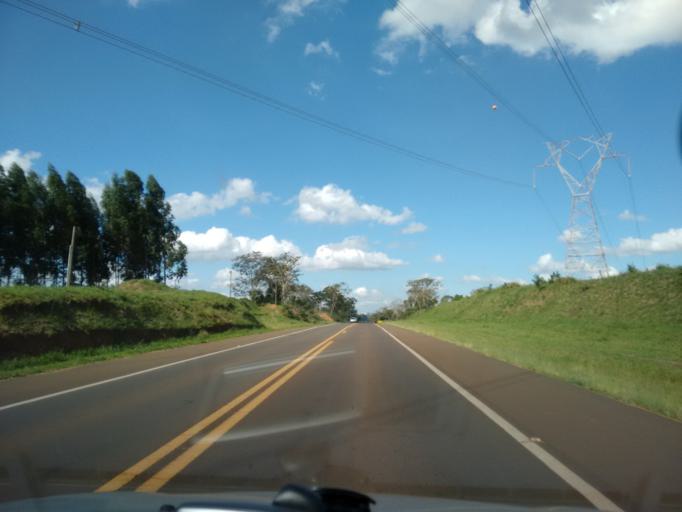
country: BR
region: Sao Paulo
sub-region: Sao Carlos
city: Sao Carlos
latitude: -22.0643
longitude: -47.9321
